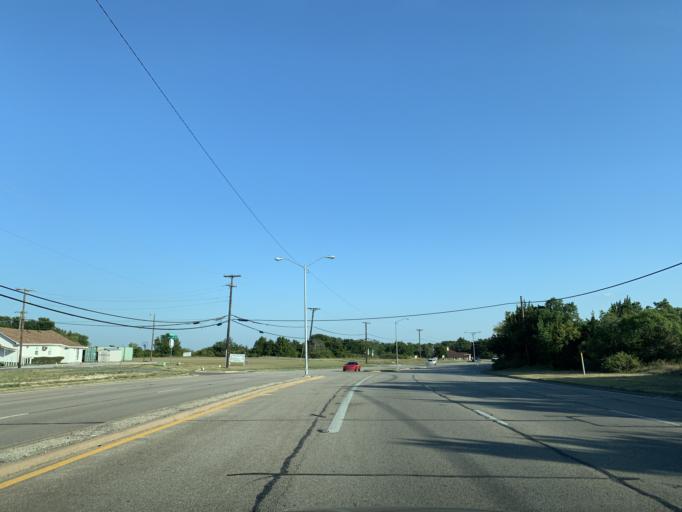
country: US
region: Texas
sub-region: Dallas County
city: Hutchins
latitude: 32.6717
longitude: -96.7835
